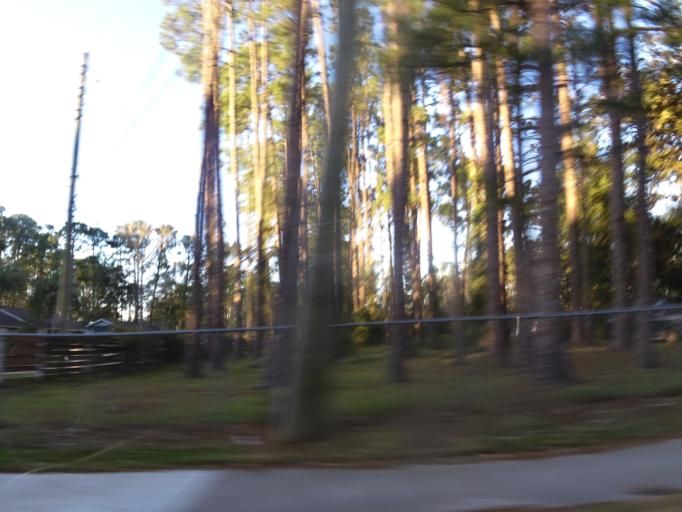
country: US
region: Florida
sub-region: Saint Johns County
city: Fruit Cove
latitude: 30.1723
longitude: -81.5862
